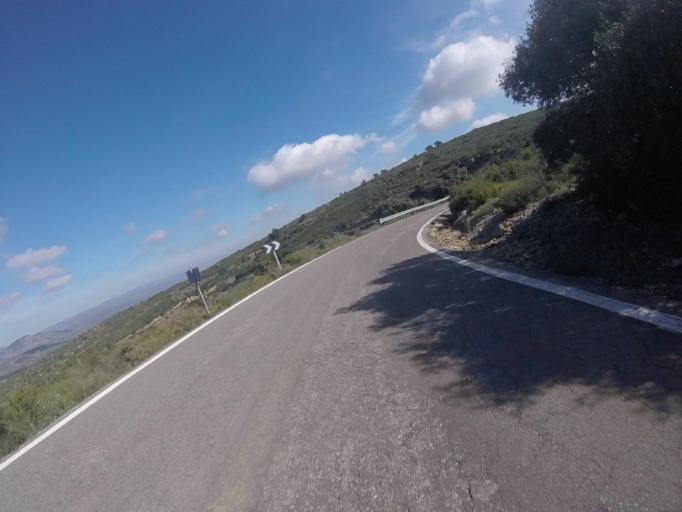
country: ES
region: Valencia
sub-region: Provincia de Castello
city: Albocasser
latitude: 40.3471
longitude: 0.0482
